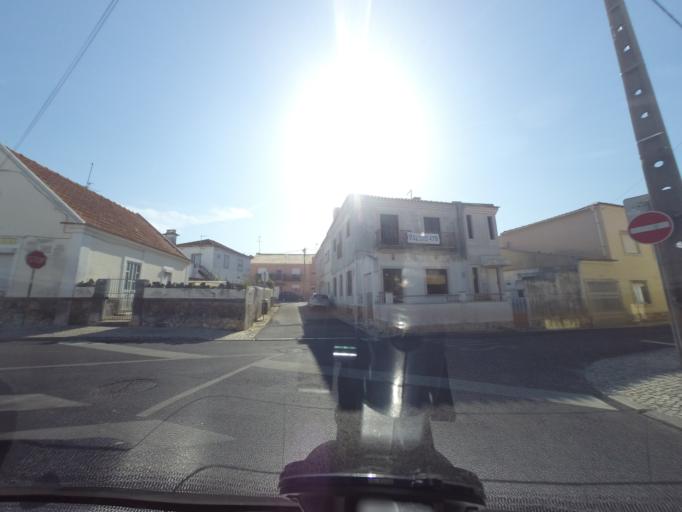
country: PT
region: Lisbon
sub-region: Cascais
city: Alcabideche
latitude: 38.7335
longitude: -9.4097
